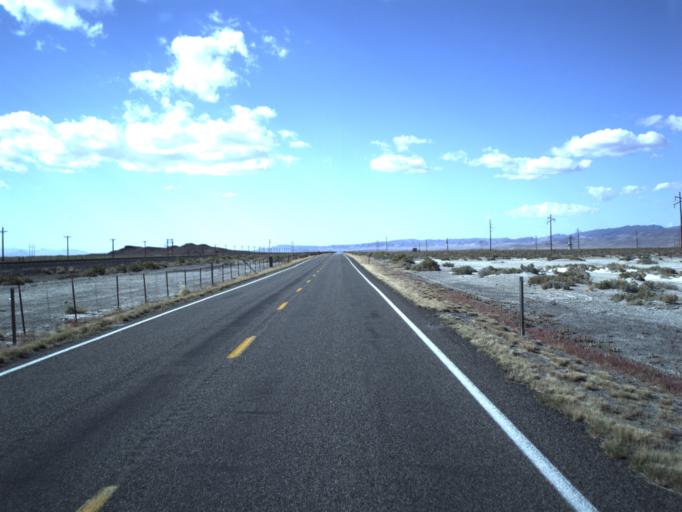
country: US
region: Utah
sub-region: Millard County
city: Delta
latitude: 39.1641
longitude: -112.7105
